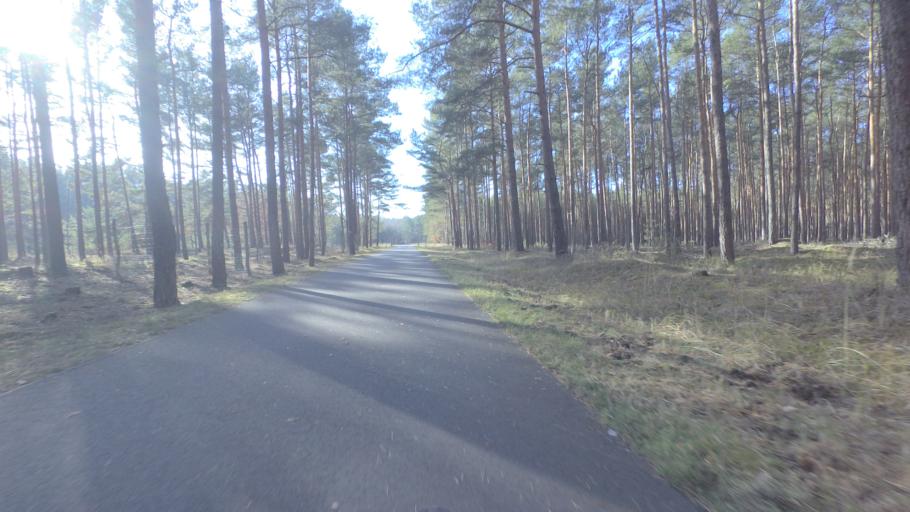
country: DE
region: Brandenburg
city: Luckenwalde
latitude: 52.0487
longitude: 13.1468
